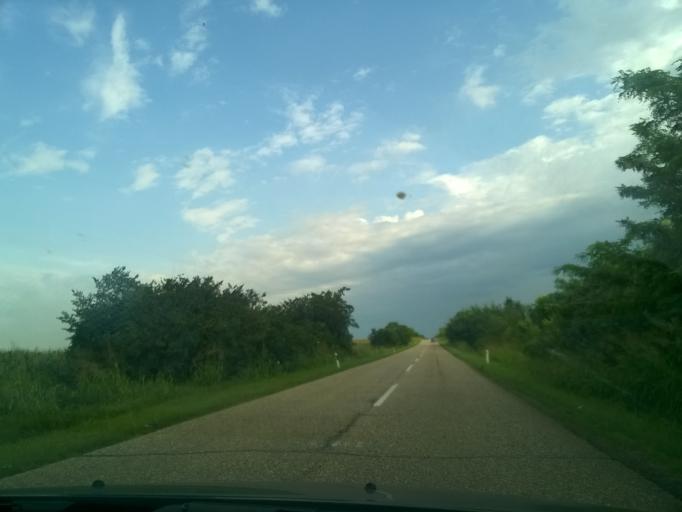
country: RS
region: Autonomna Pokrajina Vojvodina
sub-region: Juznobanatski Okrug
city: Kovacica
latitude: 45.1337
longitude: 20.6162
